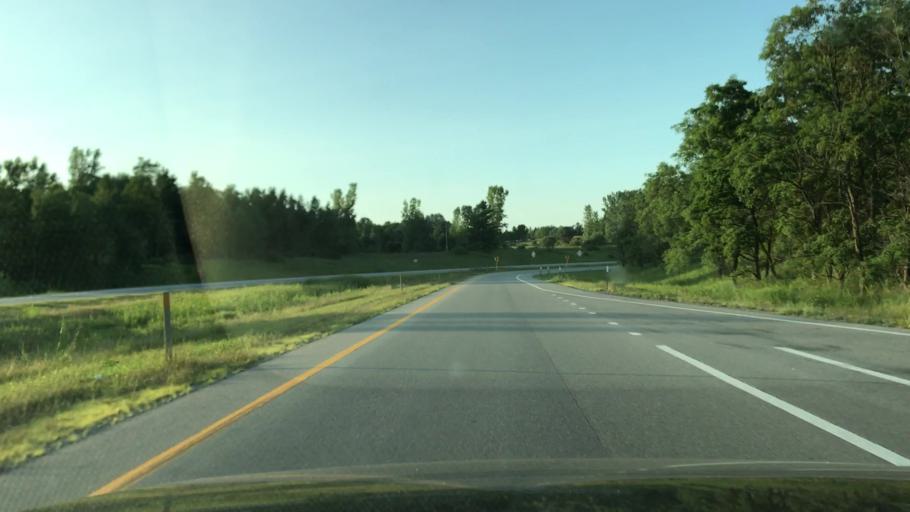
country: US
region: Michigan
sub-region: Osceola County
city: Reed City
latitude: 43.8889
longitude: -85.5318
